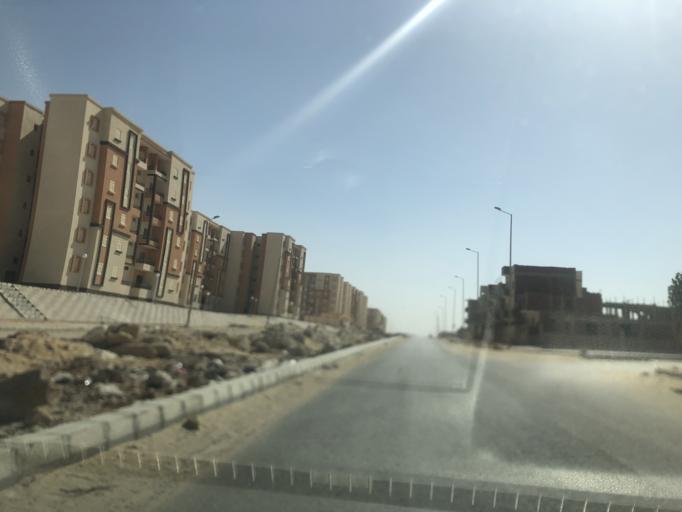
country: EG
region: Al Jizah
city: Madinat Sittah Uktubar
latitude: 29.9344
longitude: 30.9749
